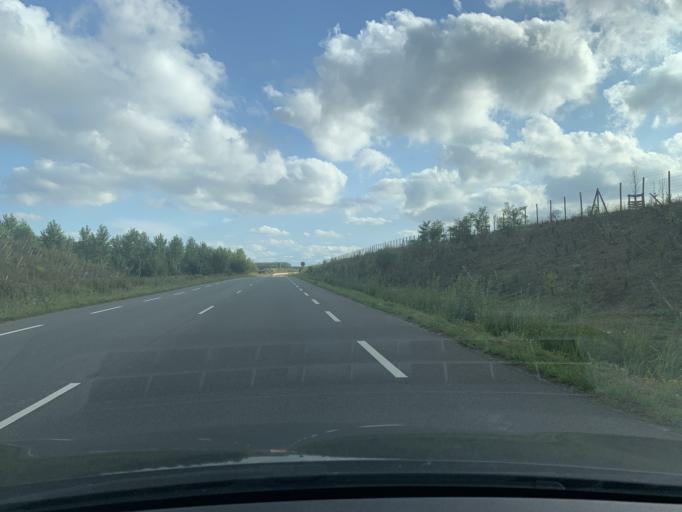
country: FR
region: Nord-Pas-de-Calais
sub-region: Departement du Nord
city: Ostricourt
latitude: 50.4492
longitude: 3.0185
